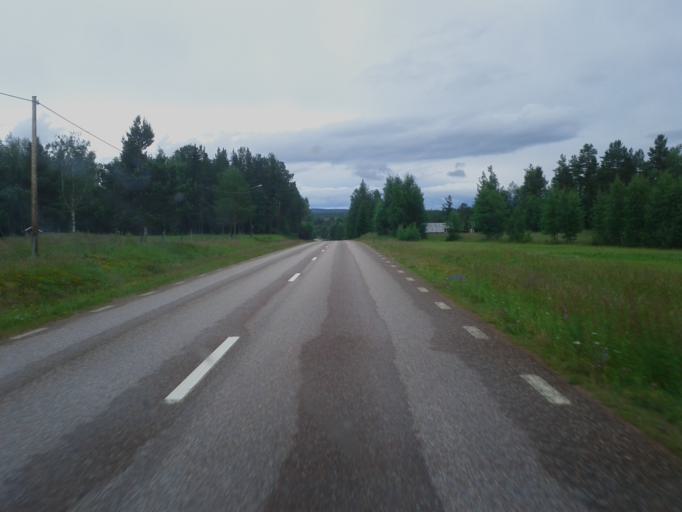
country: NO
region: Hedmark
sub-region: Trysil
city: Innbygda
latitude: 61.7297
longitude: 12.9892
